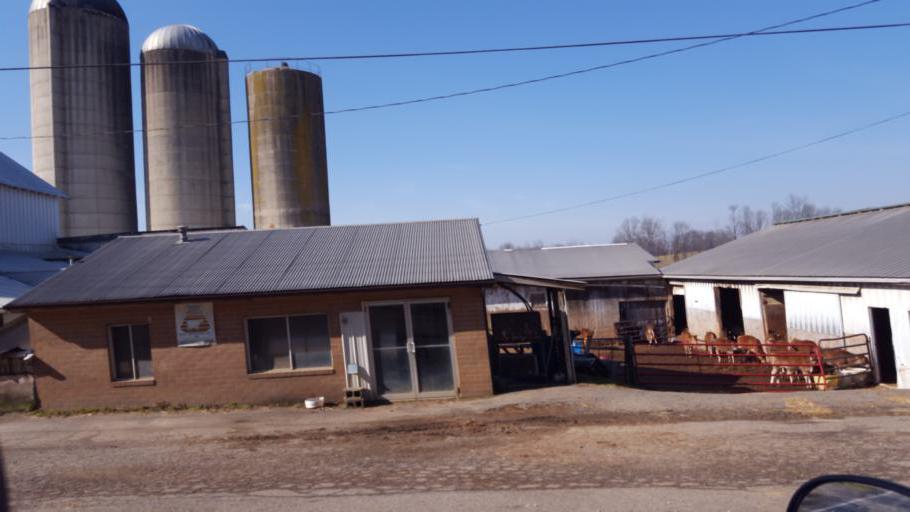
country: US
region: Ohio
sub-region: Wayne County
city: Shreve
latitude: 40.6080
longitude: -82.0244
